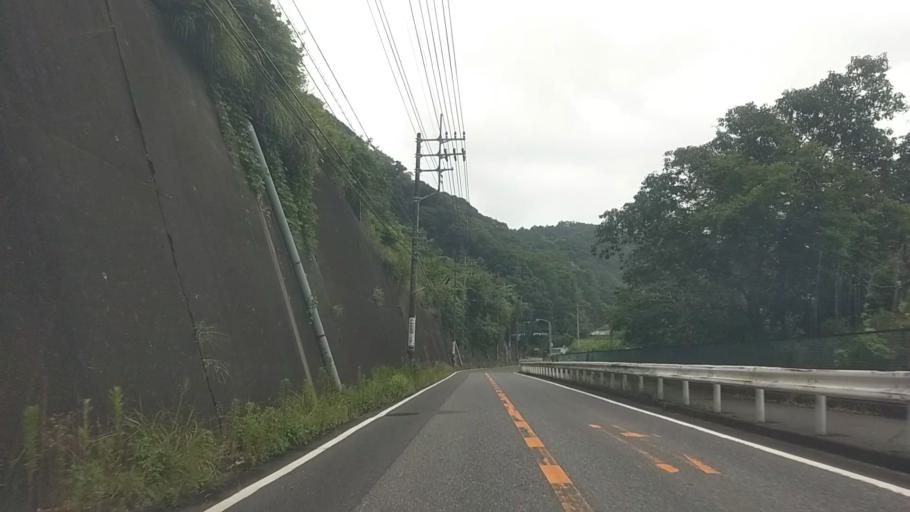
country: JP
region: Chiba
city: Kisarazu
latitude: 35.2923
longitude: 140.0819
